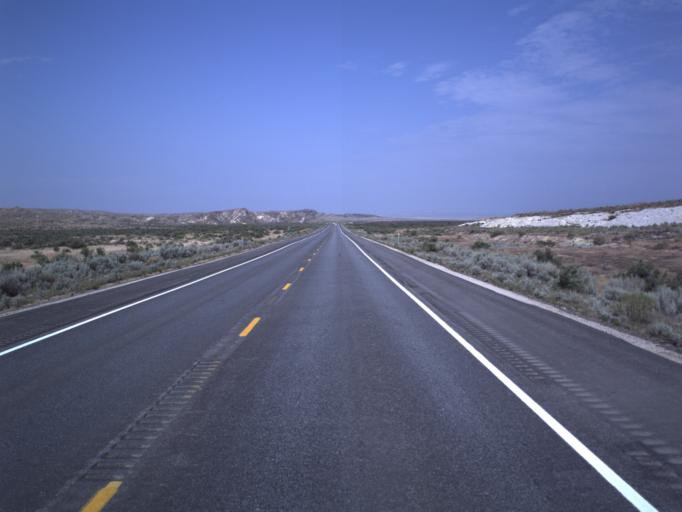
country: US
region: Colorado
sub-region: Rio Blanco County
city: Rangely
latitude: 40.2862
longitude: -109.1318
